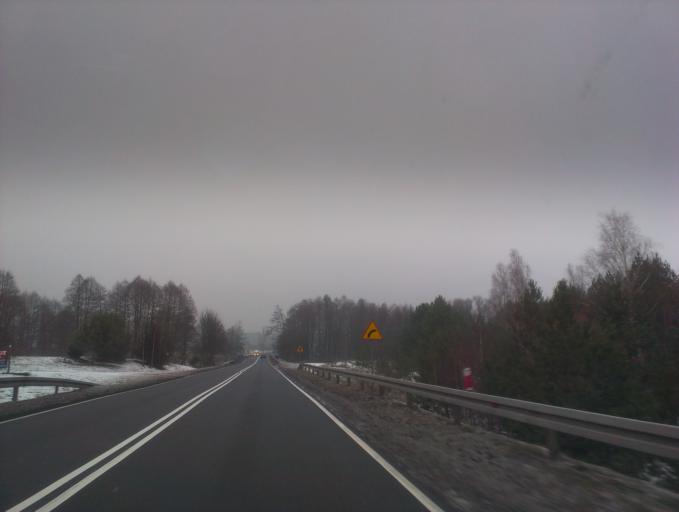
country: PL
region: Greater Poland Voivodeship
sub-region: Powiat zlotowski
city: Tarnowka
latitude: 53.2627
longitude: 16.7821
